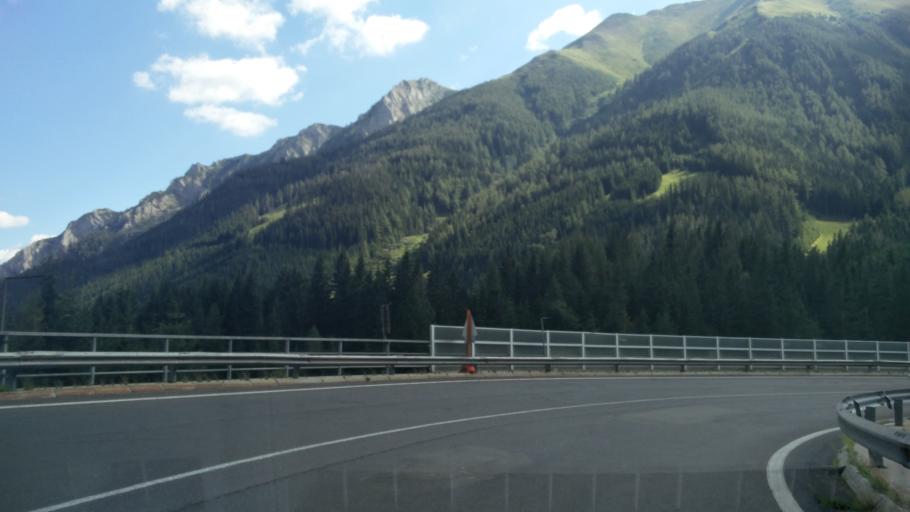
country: AT
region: Styria
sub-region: Politischer Bezirk Leoben
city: Vordernberg
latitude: 47.5172
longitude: 14.9663
